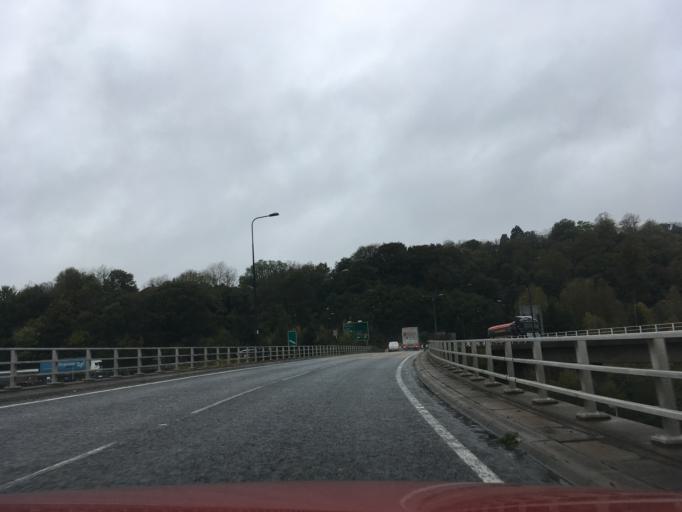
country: GB
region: Wales
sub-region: Newport
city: Newport
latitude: 51.6039
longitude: -2.9916
